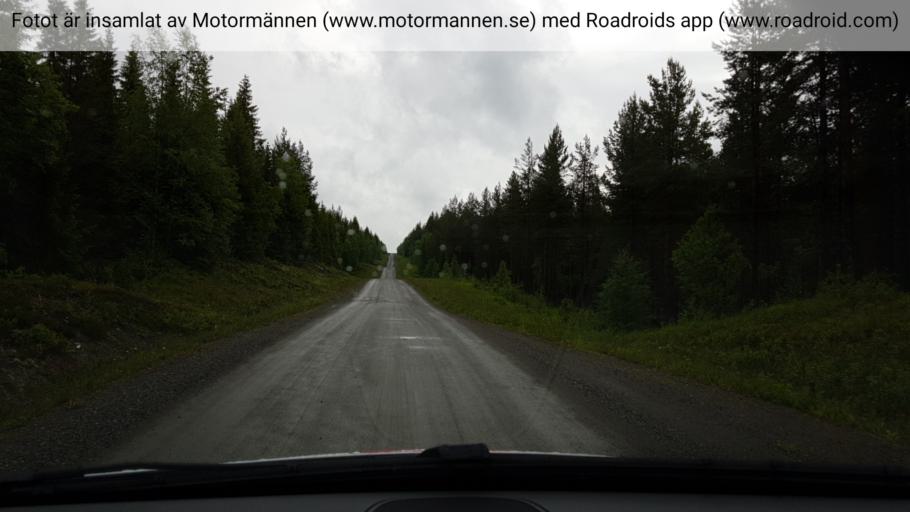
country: SE
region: Jaemtland
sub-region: Stroemsunds Kommun
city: Stroemsund
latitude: 64.2595
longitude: 15.0136
